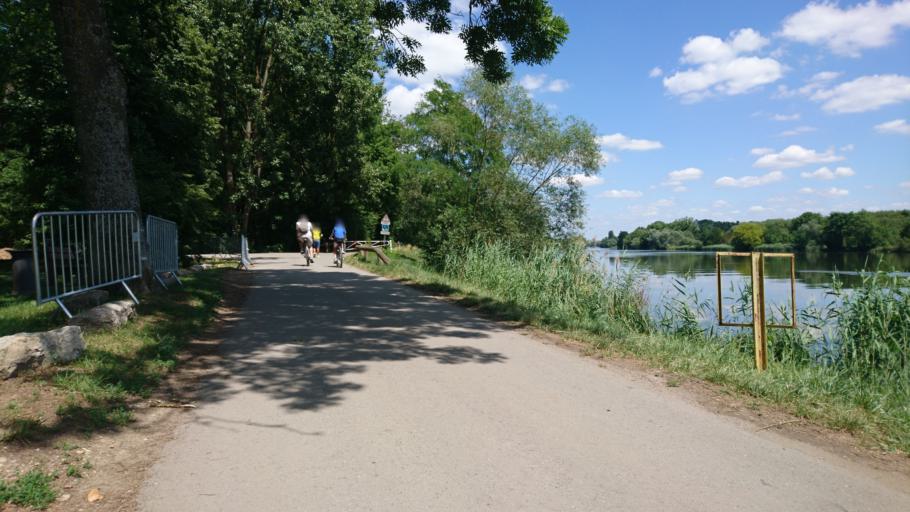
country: FR
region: Lorraine
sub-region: Departement de la Moselle
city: Moulins-les-Metz
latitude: 49.1025
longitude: 6.1150
